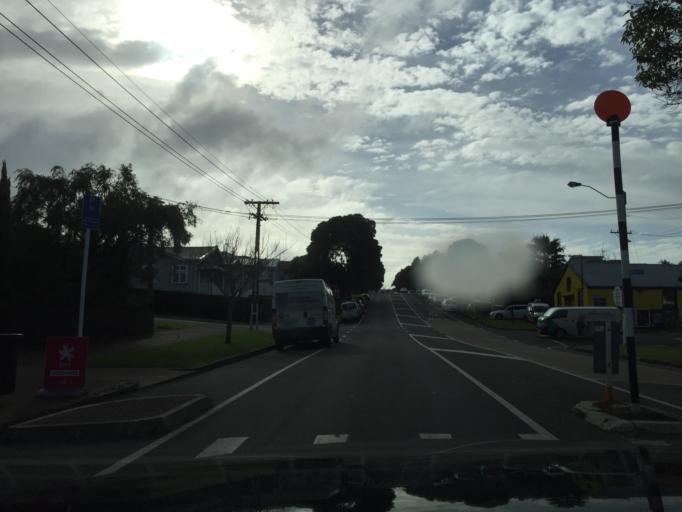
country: NZ
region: Auckland
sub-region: Auckland
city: Auckland
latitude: -36.8615
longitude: 174.7433
